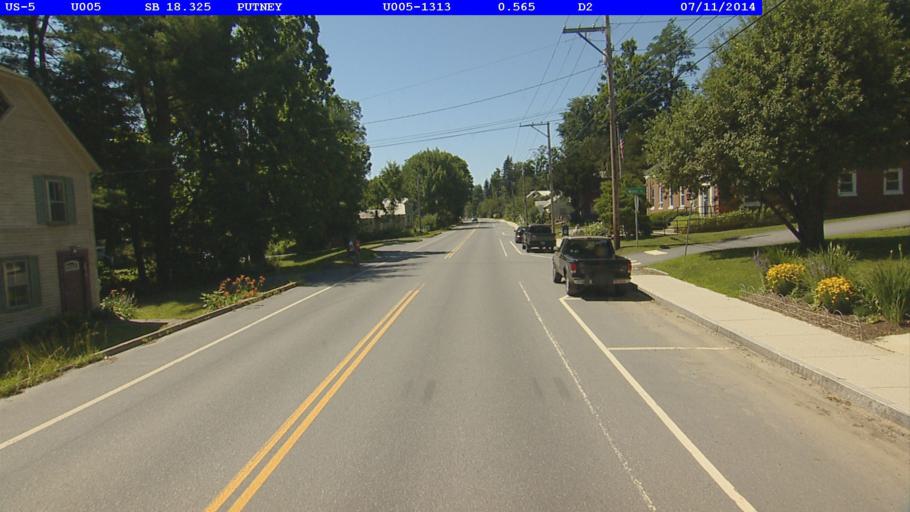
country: US
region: New Hampshire
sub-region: Cheshire County
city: Westmoreland
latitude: 42.9737
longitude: -72.5218
